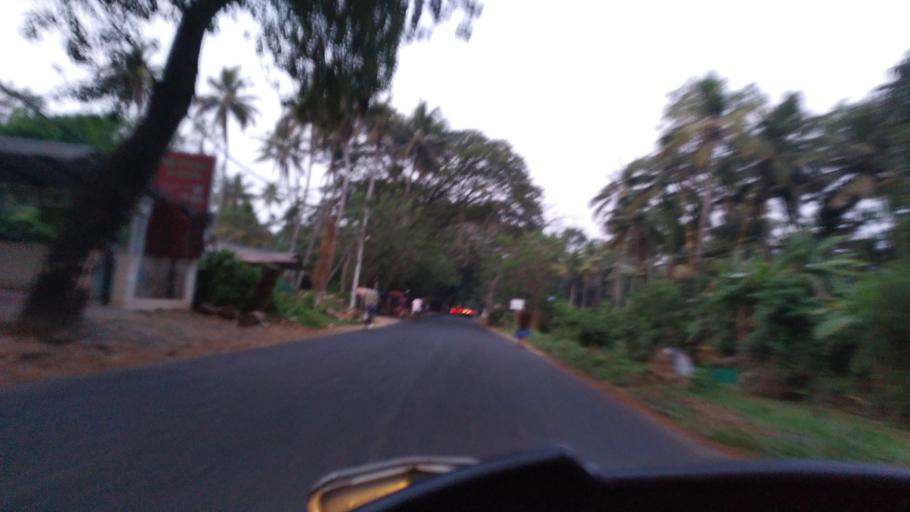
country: IN
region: Kerala
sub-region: Kottayam
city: Kottayam
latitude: 9.6039
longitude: 76.4330
